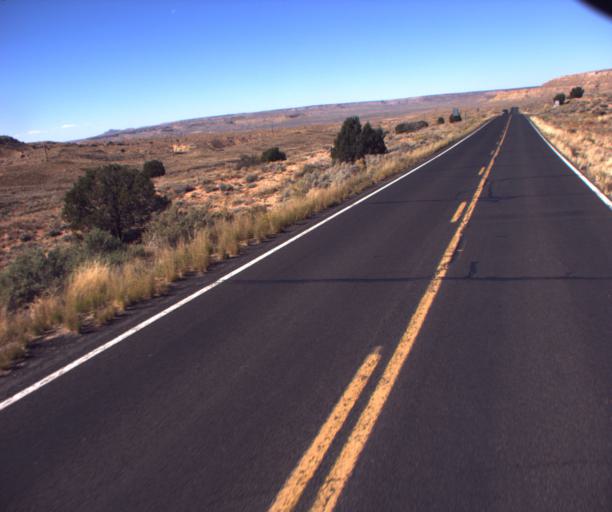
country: US
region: Arizona
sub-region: Navajo County
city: First Mesa
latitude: 35.8663
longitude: -110.5441
